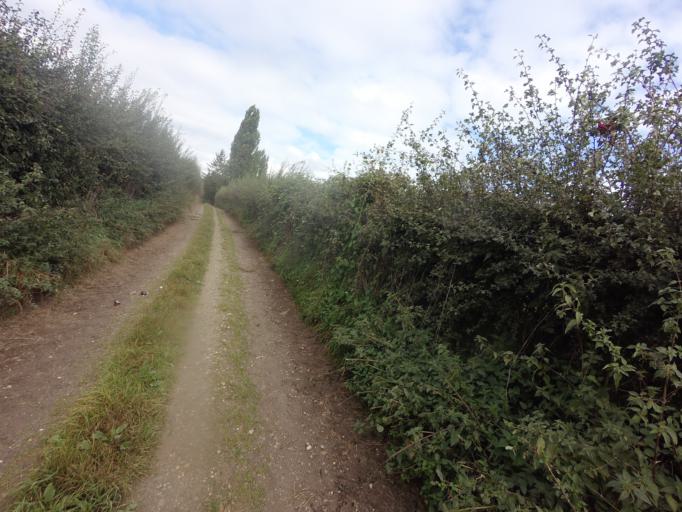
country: NL
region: Limburg
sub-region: Eijsden-Margraten
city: Margraten
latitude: 50.8137
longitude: 5.8275
